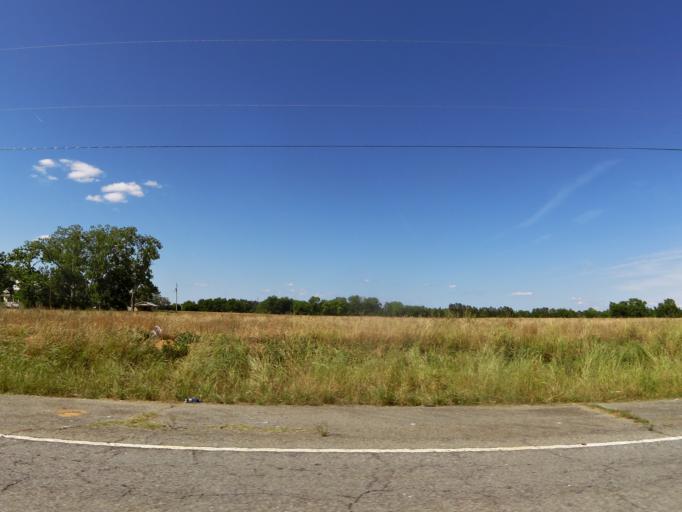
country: US
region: South Carolina
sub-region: Bamberg County
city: Denmark
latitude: 33.3393
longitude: -81.1756
